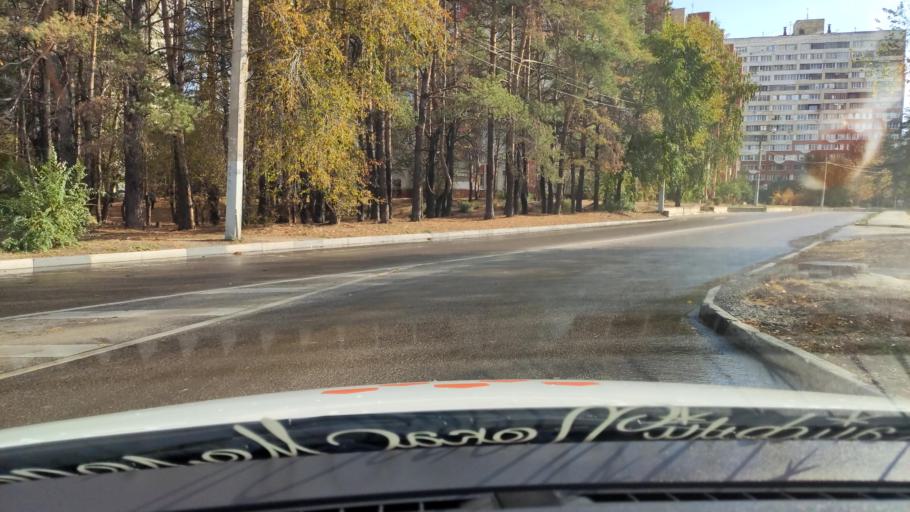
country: RU
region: Voronezj
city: Pridonskoy
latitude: 51.6863
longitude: 39.0790
